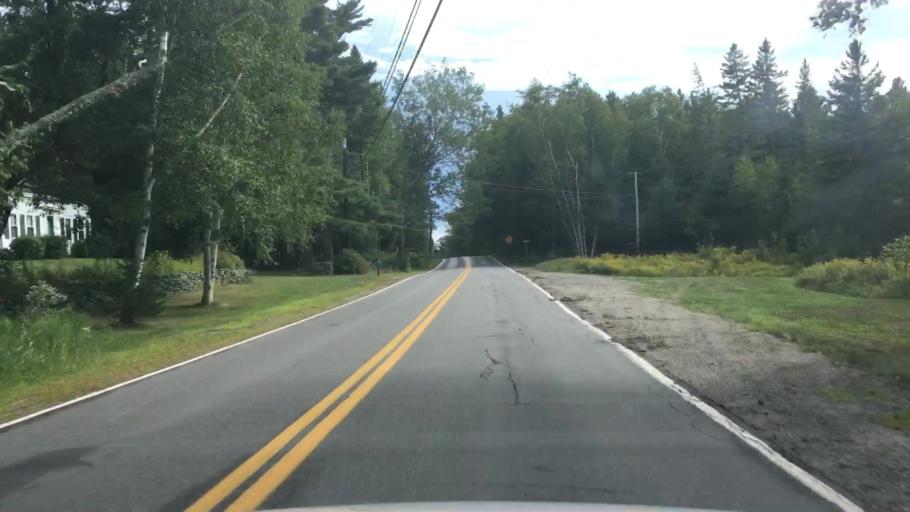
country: US
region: Maine
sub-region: Hancock County
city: Ellsworth
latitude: 44.4814
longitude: -68.4205
